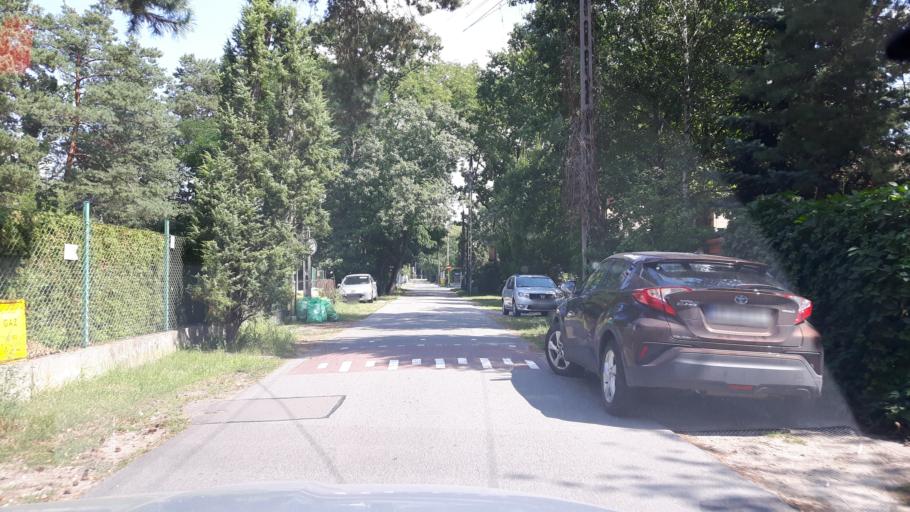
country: PL
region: Masovian Voivodeship
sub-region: Warszawa
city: Wawer
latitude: 52.2226
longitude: 21.1592
